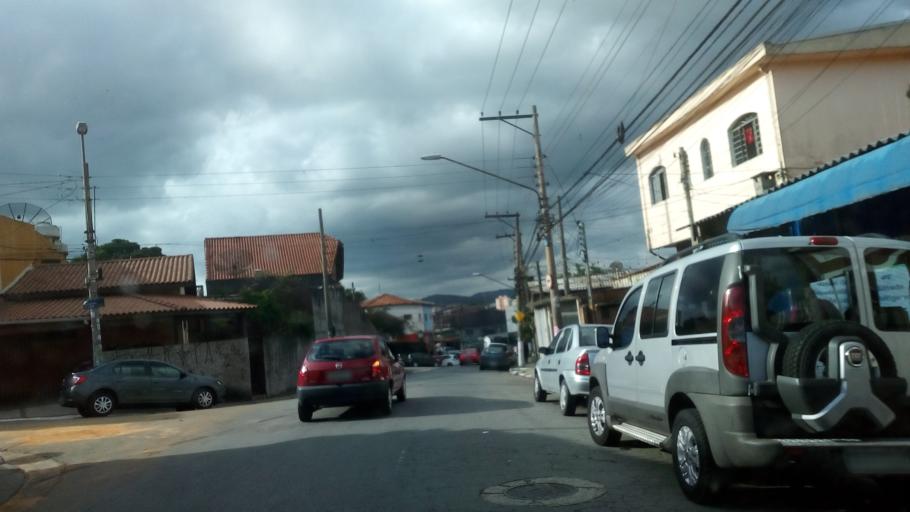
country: BR
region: Sao Paulo
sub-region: Guarulhos
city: Guarulhos
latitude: -23.4595
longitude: -46.5212
